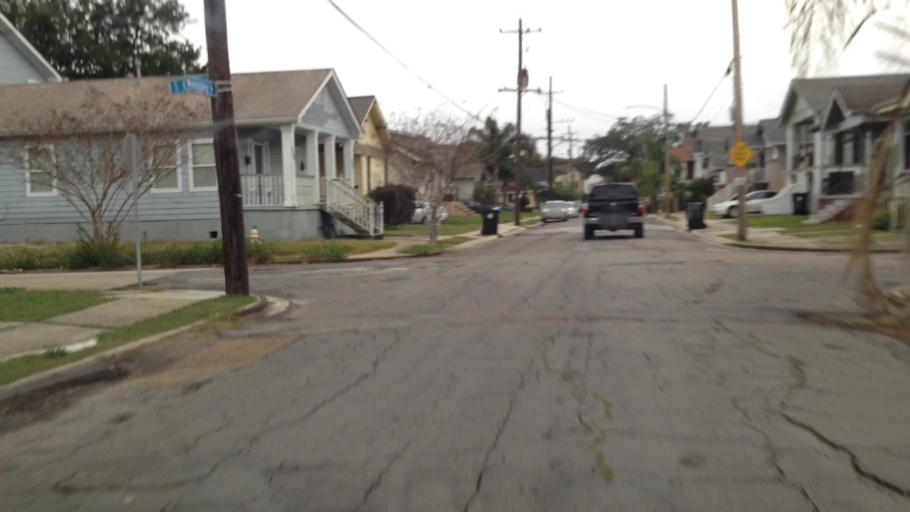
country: US
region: Louisiana
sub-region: Orleans Parish
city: New Orleans
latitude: 29.9517
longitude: -90.1054
